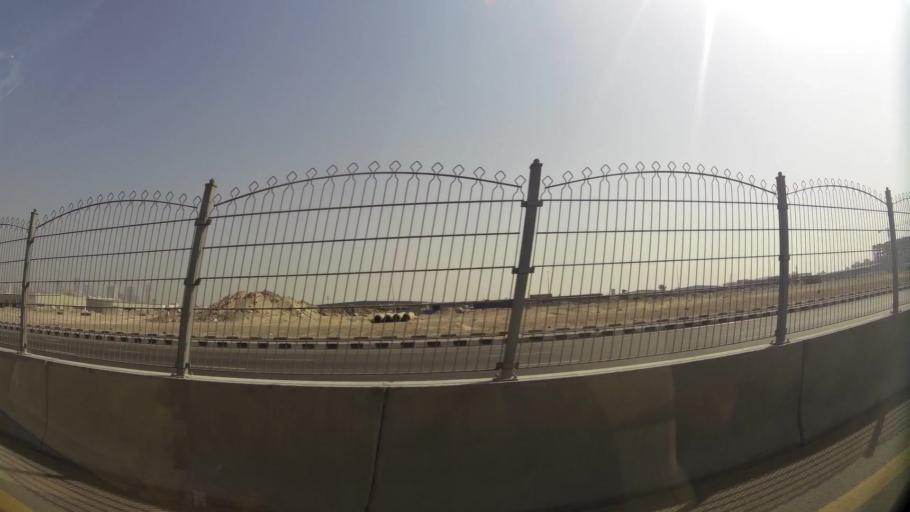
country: AE
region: Ash Shariqah
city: Sharjah
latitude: 25.3012
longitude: 55.3902
